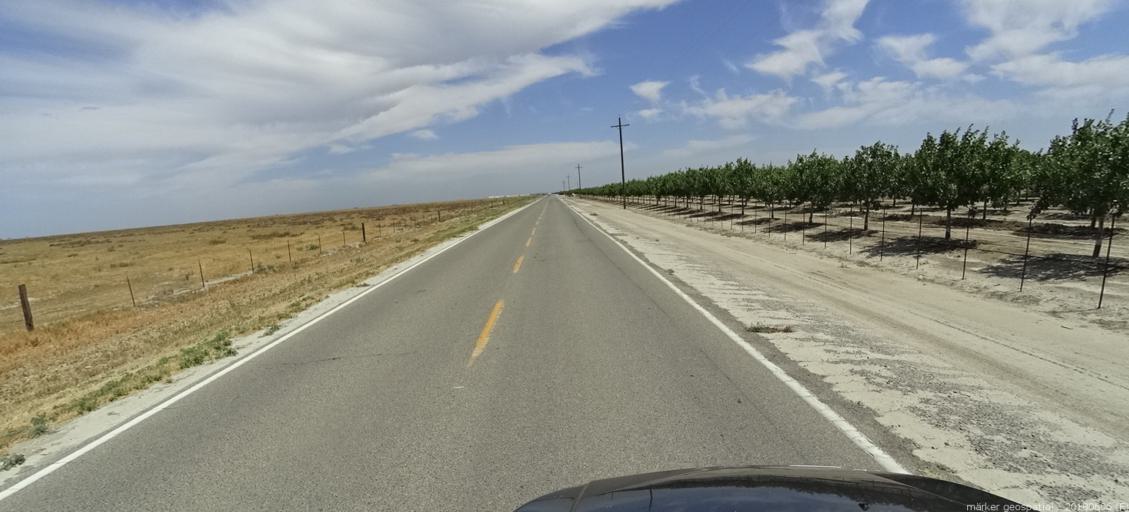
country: US
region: California
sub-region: Fresno County
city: Firebaugh
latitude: 36.8871
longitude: -120.3819
